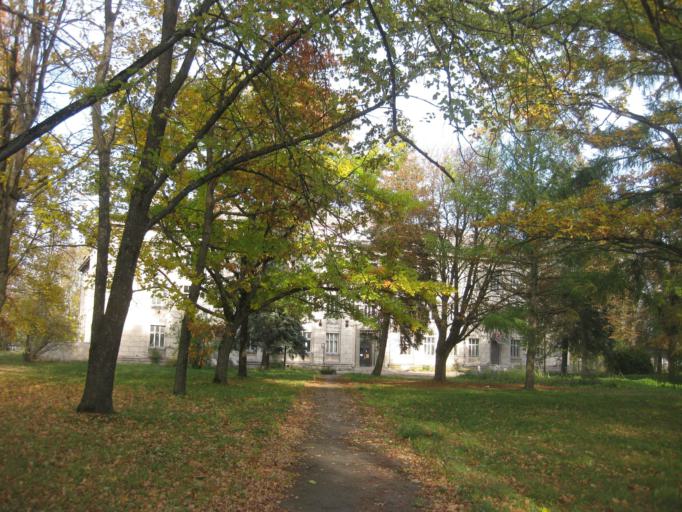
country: LT
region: Kauno apskritis
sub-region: Kaunas
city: Aleksotas
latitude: 54.8916
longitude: 23.8797
